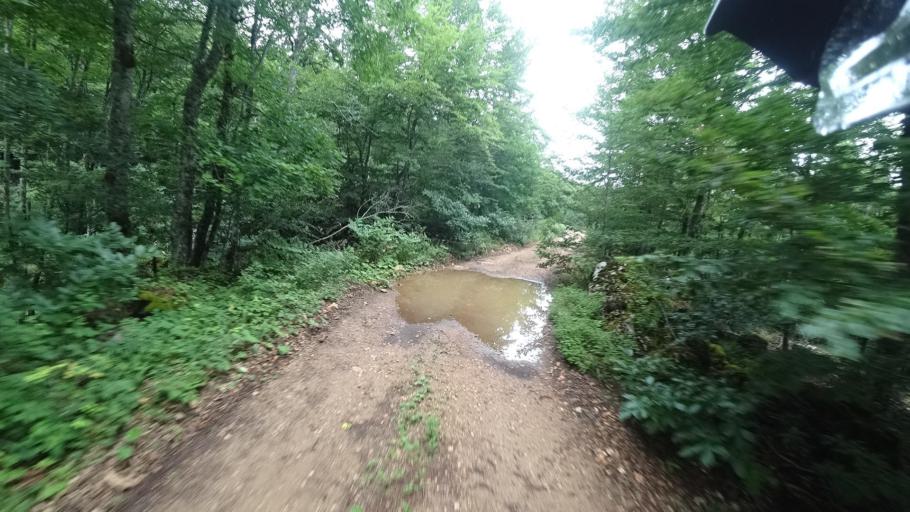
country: BA
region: Federation of Bosnia and Herzegovina
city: Bihac
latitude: 44.6292
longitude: 15.7929
